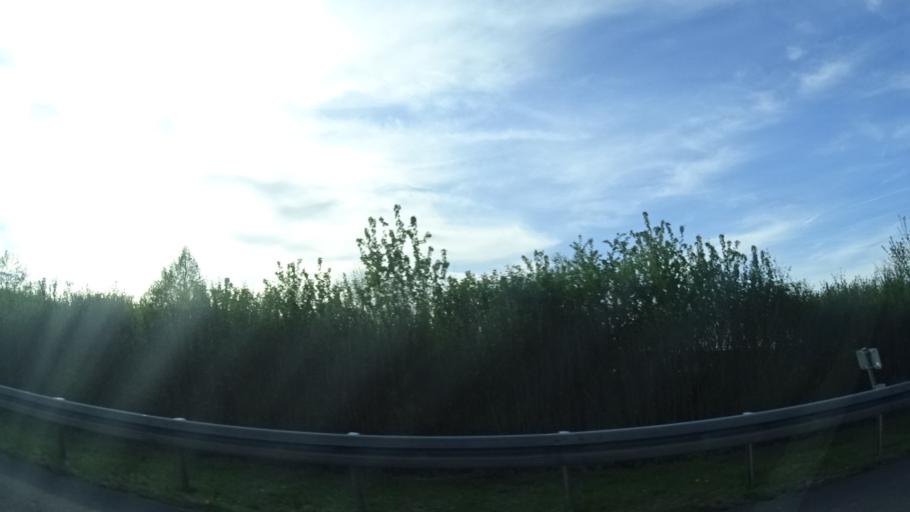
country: DE
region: Baden-Wuerttemberg
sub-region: Regierungsbezirk Stuttgart
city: Grossrinderfeld
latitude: 49.6809
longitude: 9.7799
